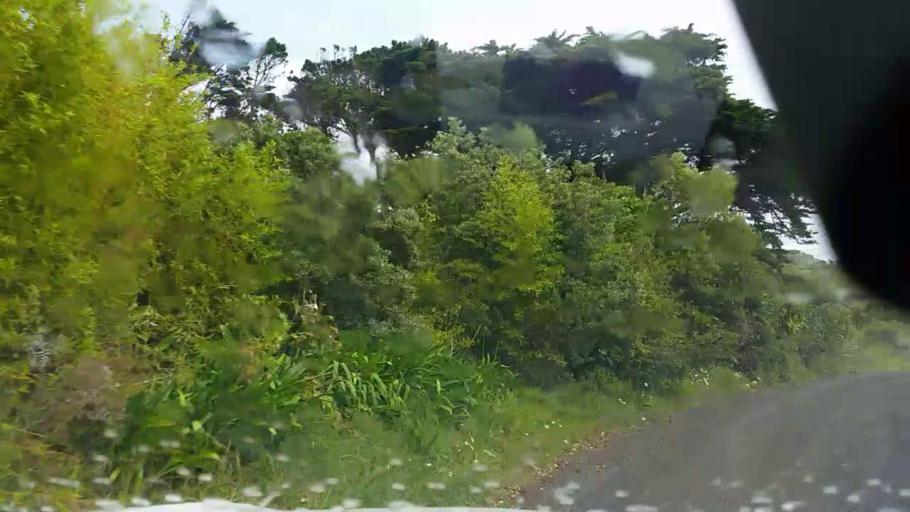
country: NZ
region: Auckland
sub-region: Auckland
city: Muriwai Beach
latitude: -36.9278
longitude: 174.4595
